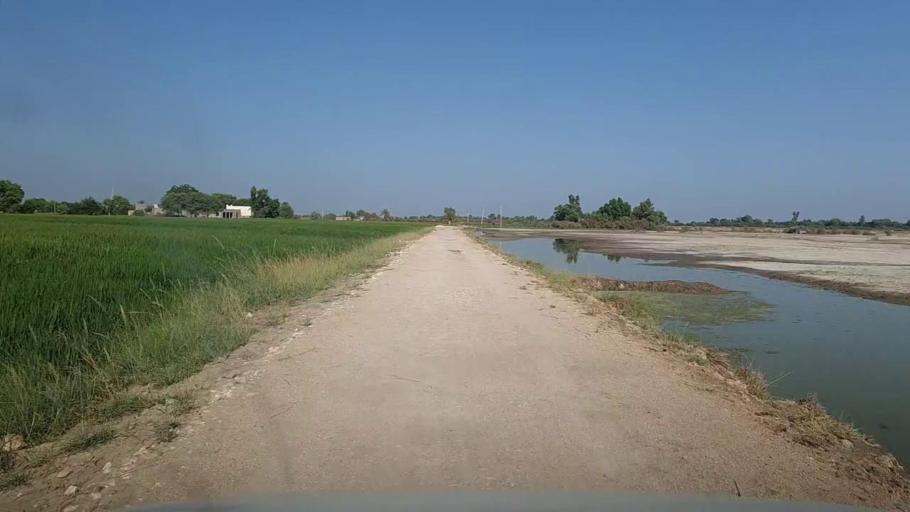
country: PK
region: Sindh
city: Kandhkot
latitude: 28.2626
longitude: 69.3314
